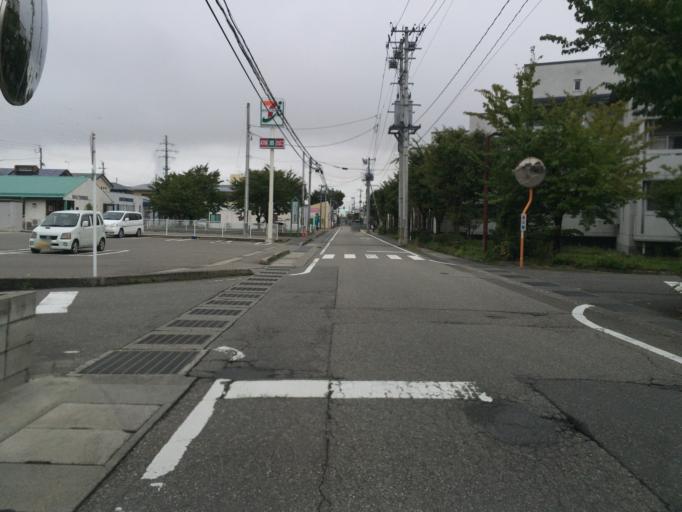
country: JP
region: Fukushima
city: Kitakata
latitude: 37.4763
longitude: 139.9113
